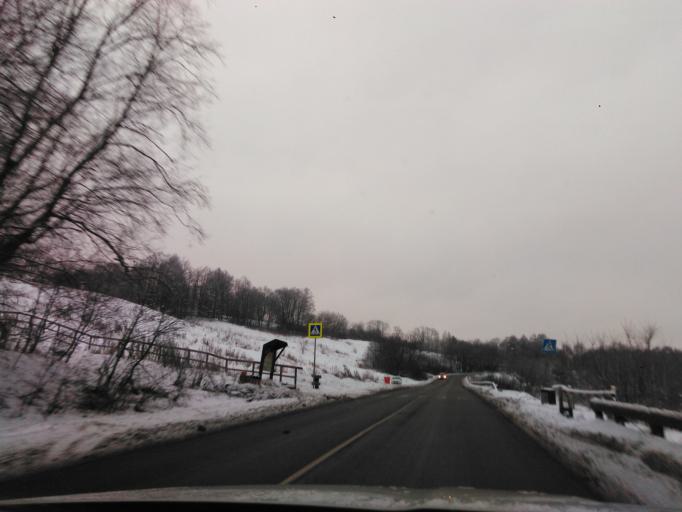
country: RU
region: Moscow
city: Khimki
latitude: 55.8909
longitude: 37.3755
